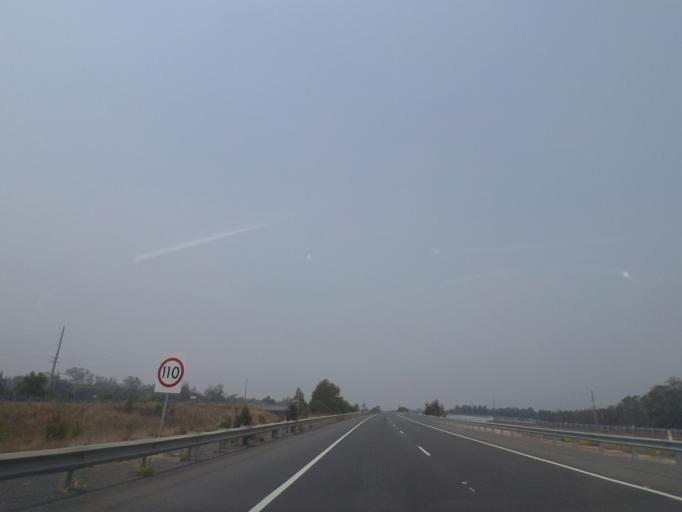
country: AU
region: New South Wales
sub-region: Ballina
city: Ballina
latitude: -28.8659
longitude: 153.4997
